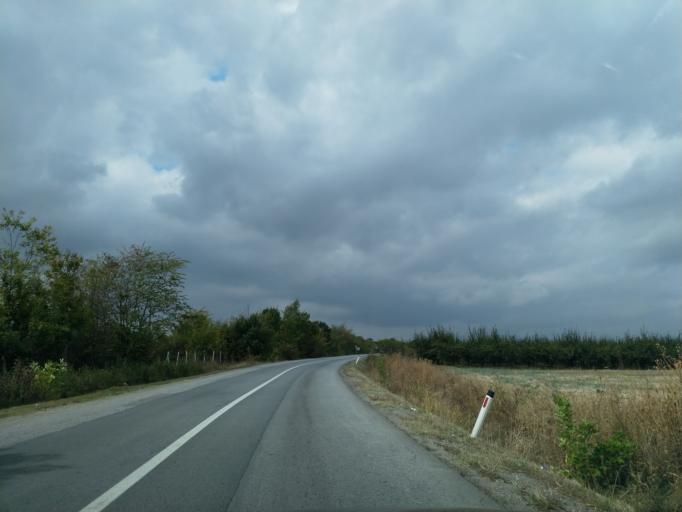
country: RS
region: Central Serbia
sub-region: Sumadijski Okrug
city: Kragujevac
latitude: 44.1269
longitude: 20.8175
